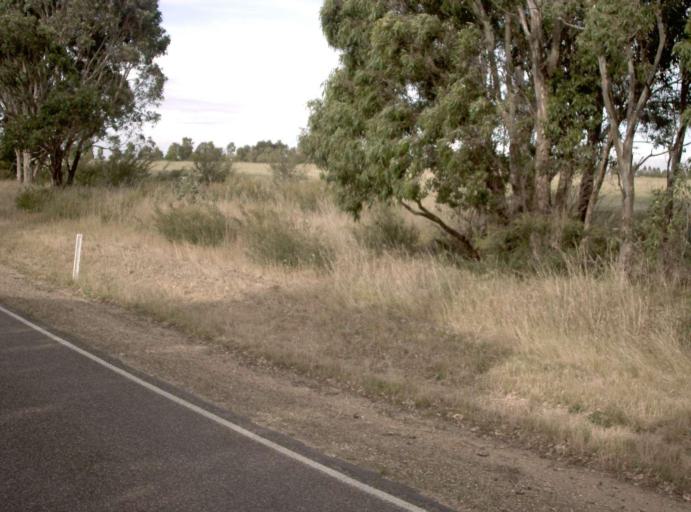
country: AU
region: Victoria
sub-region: Wellington
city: Heyfield
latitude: -38.0428
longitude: 146.6654
